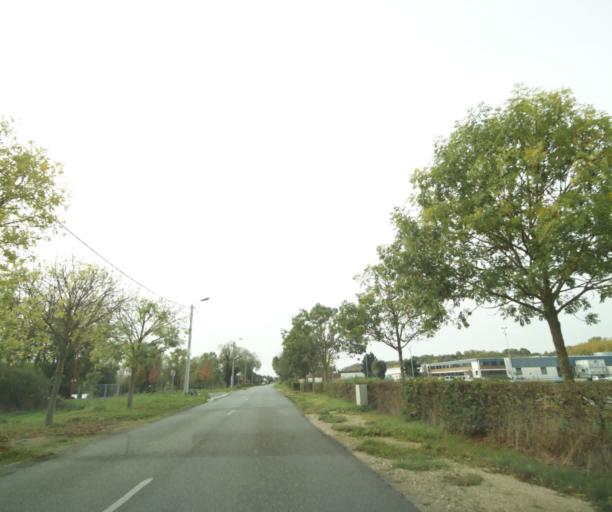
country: FR
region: Centre
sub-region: Departement d'Eure-et-Loir
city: Luray
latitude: 48.7514
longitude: 1.3948
